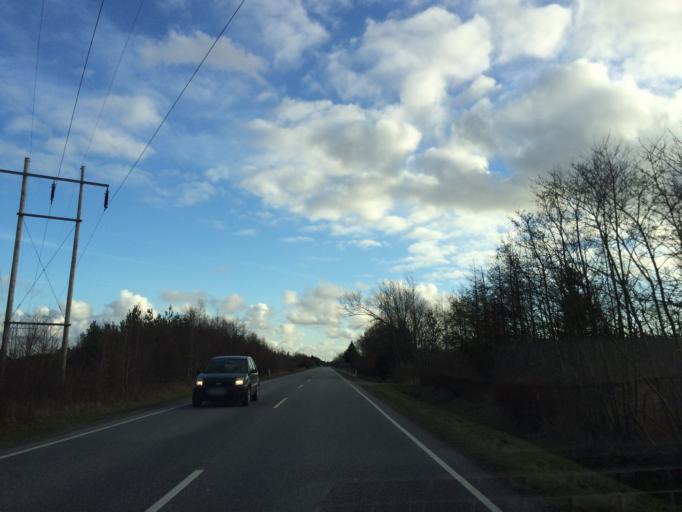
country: DK
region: Central Jutland
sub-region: Holstebro Kommune
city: Ulfborg
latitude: 56.3767
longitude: 8.3295
